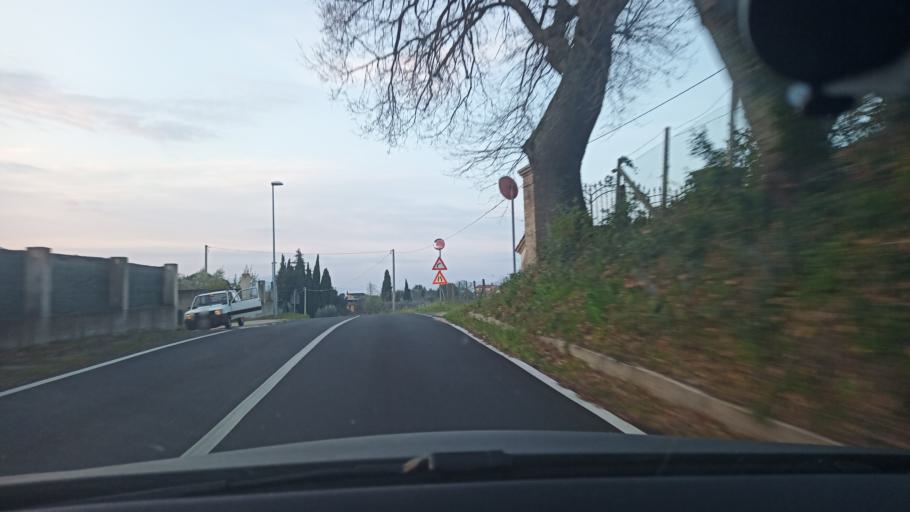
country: IT
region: Latium
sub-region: Provincia di Rieti
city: Torri in Sabina
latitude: 42.3441
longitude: 12.6512
